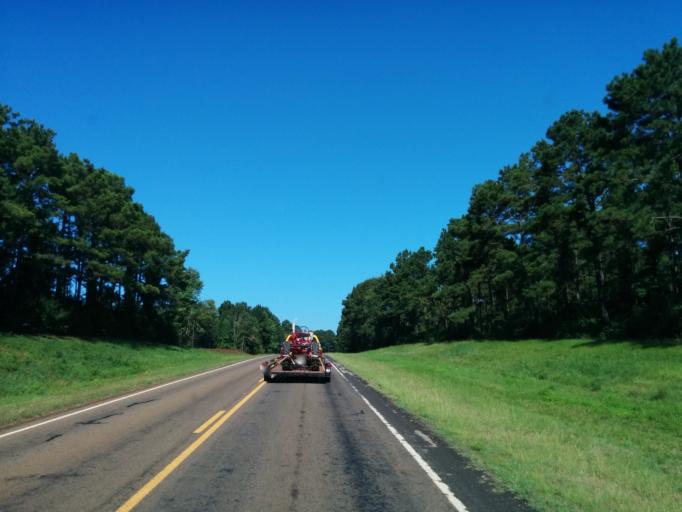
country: US
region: Texas
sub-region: Sabine County
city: Milam
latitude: 31.4291
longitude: -93.8062
